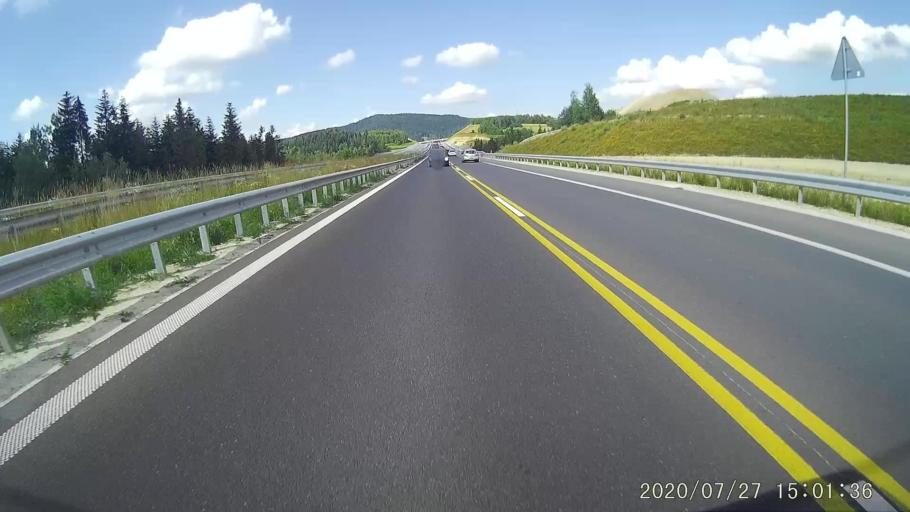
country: PL
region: Lesser Poland Voivodeship
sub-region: Powiat suski
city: Letownia
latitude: 49.6798
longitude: 19.8910
